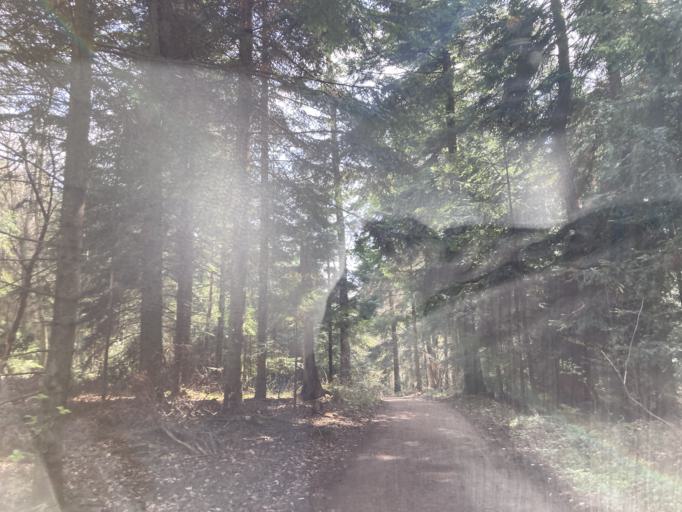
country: DE
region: Baden-Wuerttemberg
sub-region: Karlsruhe Region
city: Dobel
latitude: 48.8380
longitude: 8.5217
